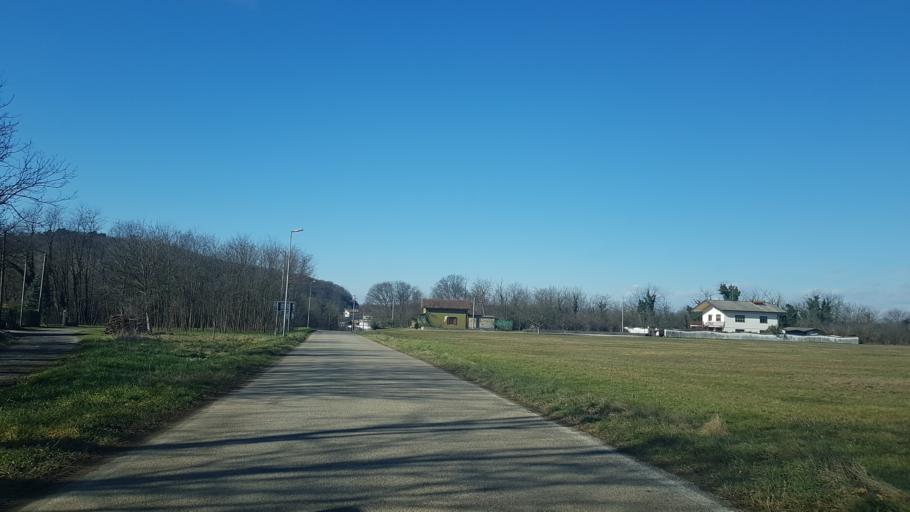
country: IT
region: Friuli Venezia Giulia
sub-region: Provincia di Gorizia
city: Savogna d'Isonzo
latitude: 45.8967
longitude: 13.5777
